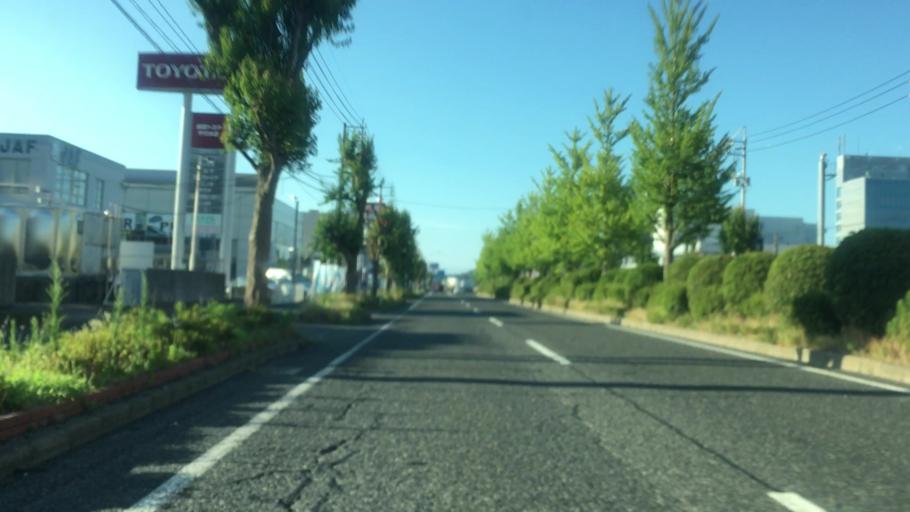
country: JP
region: Tottori
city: Tottori
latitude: 35.5143
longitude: 134.2020
